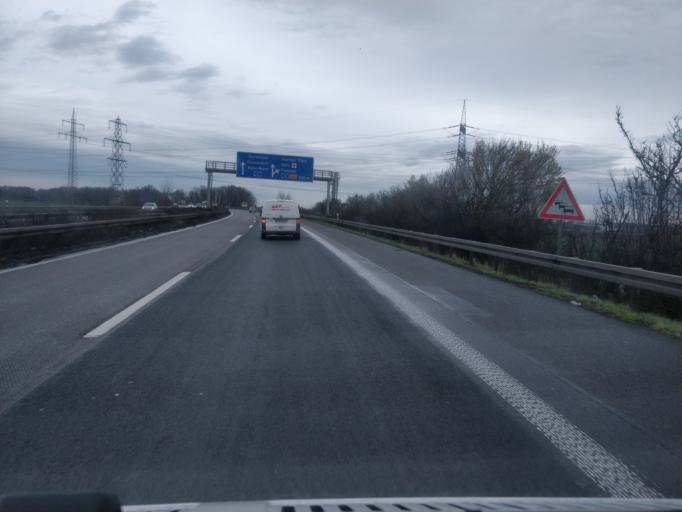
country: DE
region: North Rhine-Westphalia
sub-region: Regierungsbezirk Koln
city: Frechen
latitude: 50.9067
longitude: 6.8470
